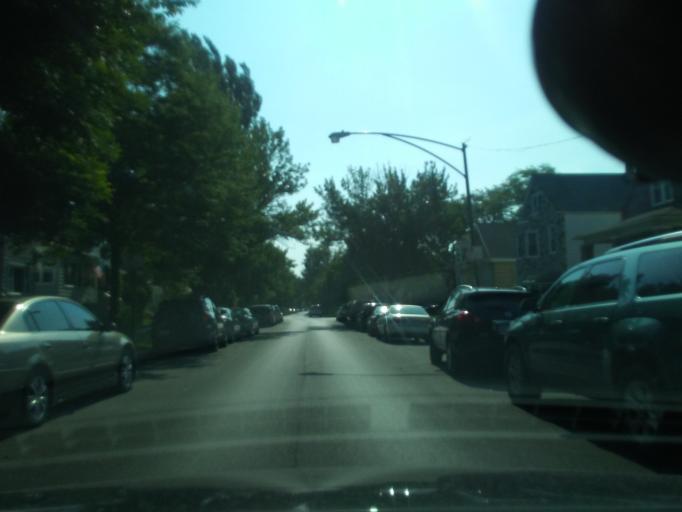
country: US
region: Illinois
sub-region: Cook County
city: Elmwood Park
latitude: 41.9277
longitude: -87.7621
